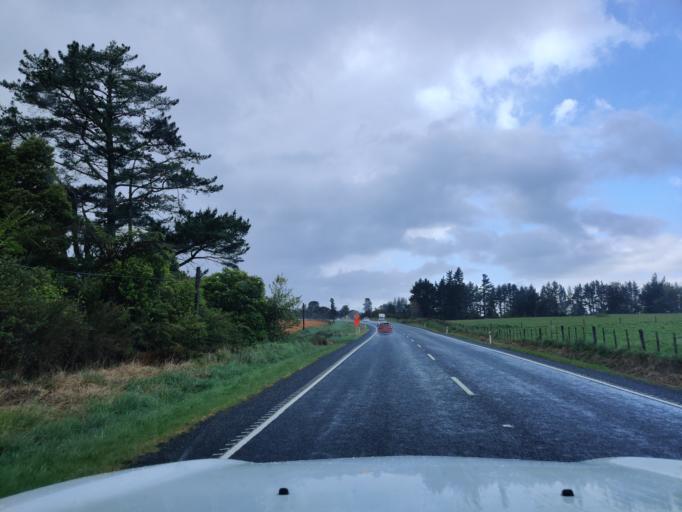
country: NZ
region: Waikato
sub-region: Matamata-Piako District
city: Matamata
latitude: -37.9990
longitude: 175.8672
